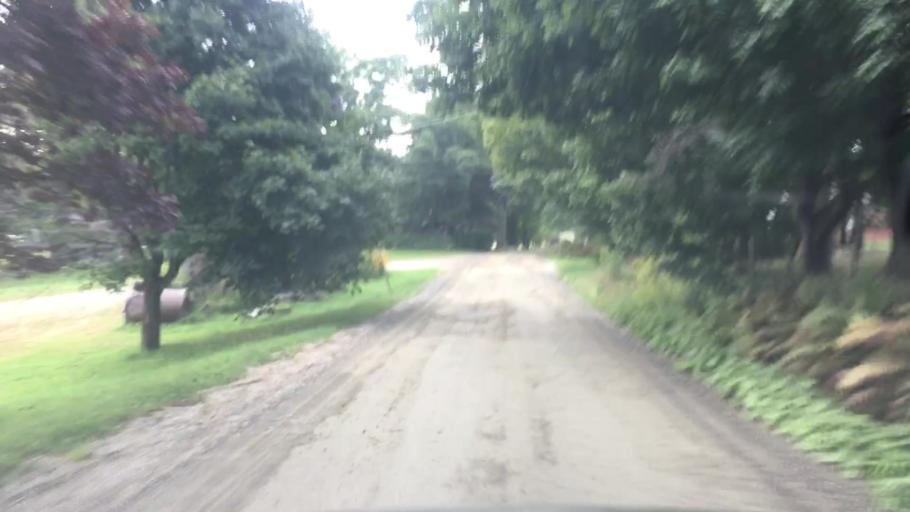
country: US
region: Vermont
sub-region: Windham County
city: Dover
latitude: 42.8338
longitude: -72.8018
